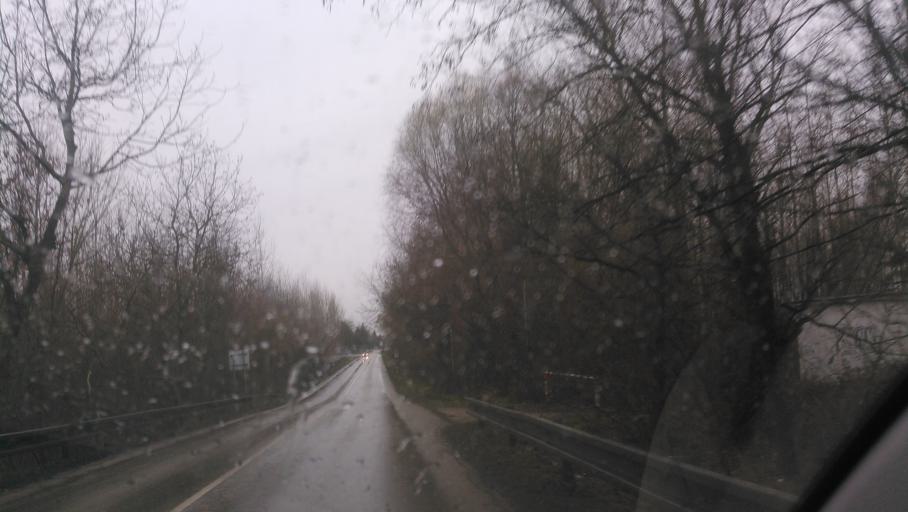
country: SK
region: Nitriansky
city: Kolarovo
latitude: 47.9296
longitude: 17.9810
